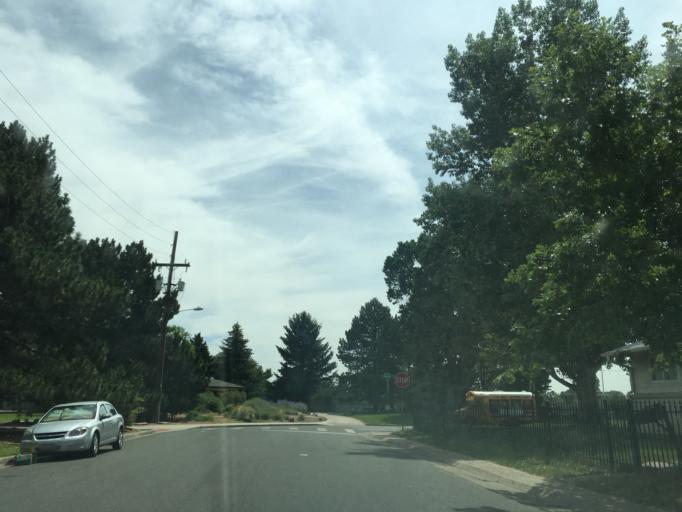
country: US
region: Colorado
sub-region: Jefferson County
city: Lakewood
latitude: 39.6949
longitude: -105.0372
